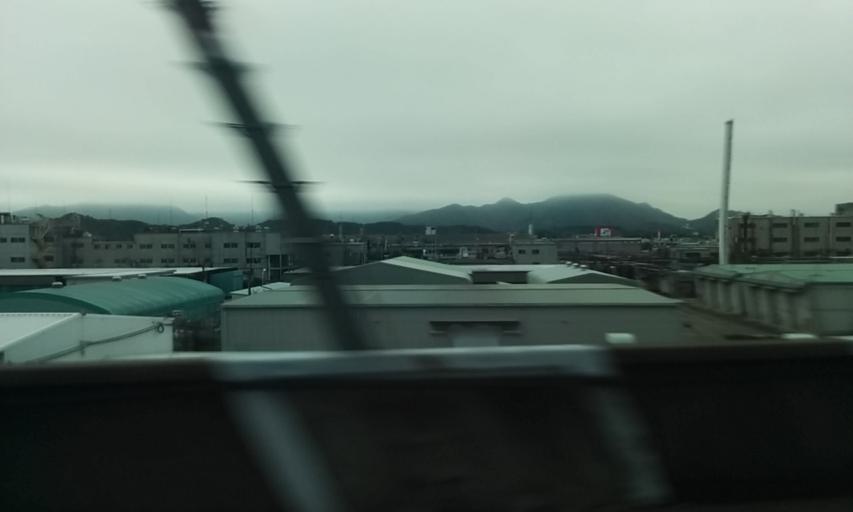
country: JP
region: Hyogo
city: Tatsunocho-tominaga
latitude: 34.8245
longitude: 134.5357
